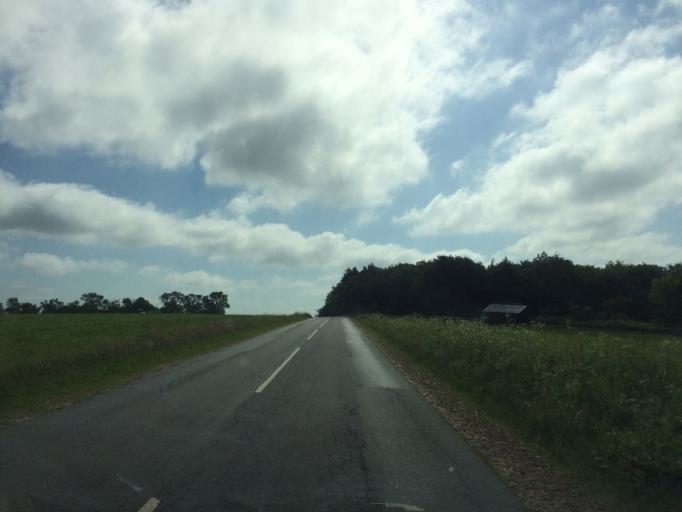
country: DK
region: Central Jutland
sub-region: Ringkobing-Skjern Kommune
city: Videbaek
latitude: 56.2042
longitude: 8.4980
